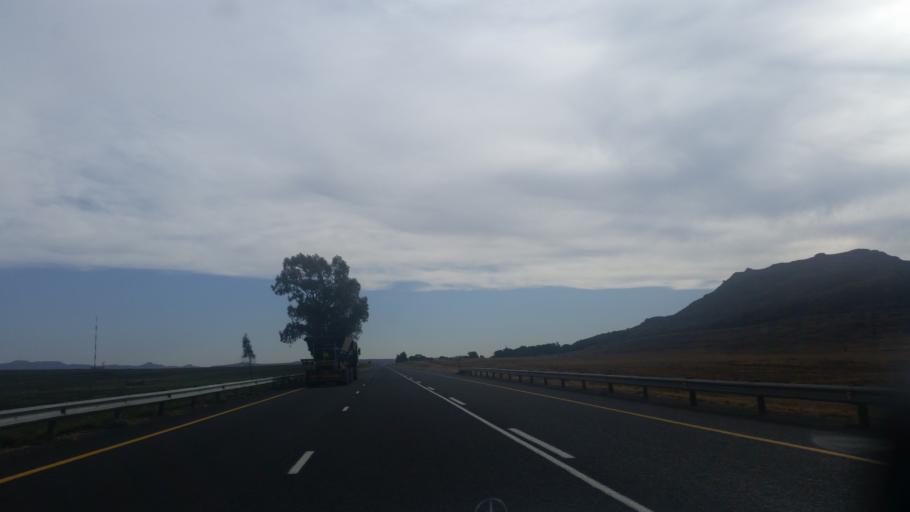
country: ZA
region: Orange Free State
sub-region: Thabo Mofutsanyana District Municipality
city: Phuthaditjhaba
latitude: -28.3025
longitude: 28.7880
